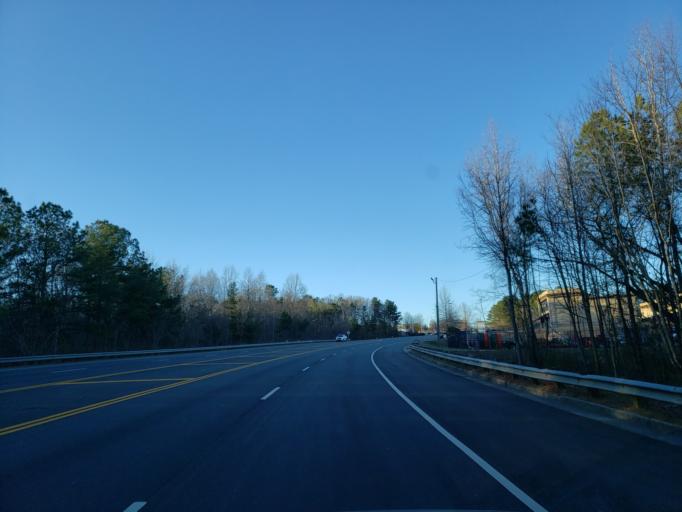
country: US
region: Georgia
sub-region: Cherokee County
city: Holly Springs
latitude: 34.1931
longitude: -84.5091
